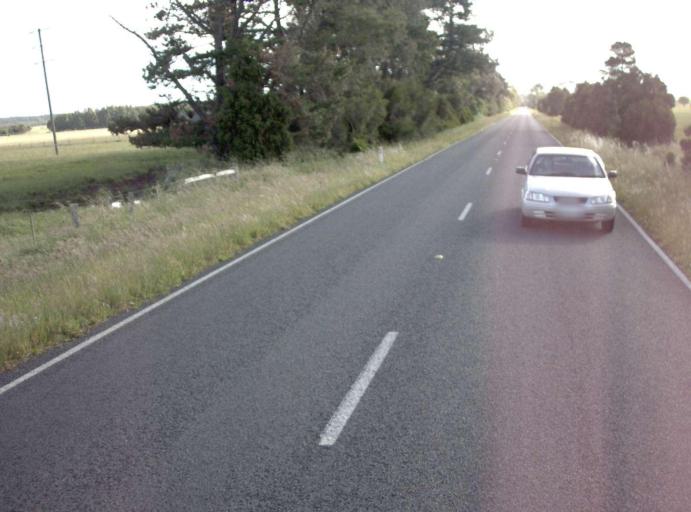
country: AU
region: Victoria
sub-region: Bass Coast
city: North Wonthaggi
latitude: -38.5398
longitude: 145.8628
